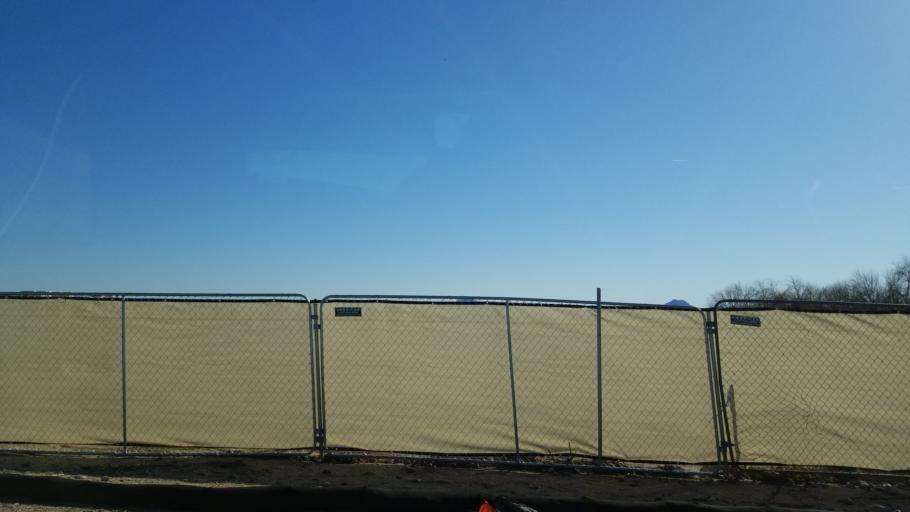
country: US
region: Arizona
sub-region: Maricopa County
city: Paradise Valley
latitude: 33.6555
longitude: -111.9378
